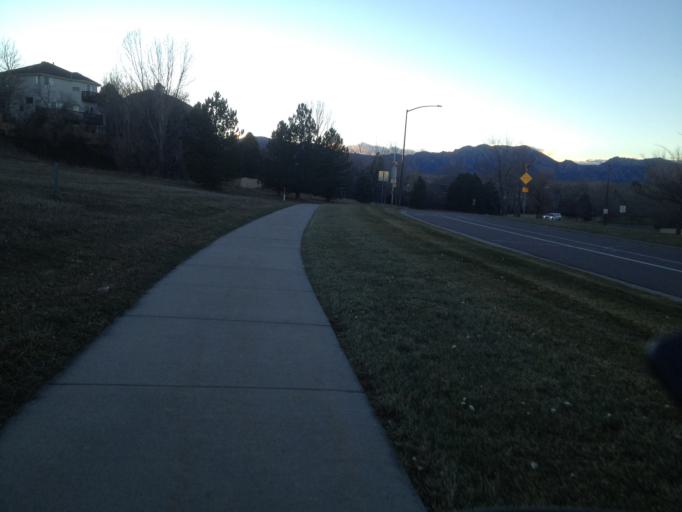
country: US
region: Colorado
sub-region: Boulder County
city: Superior
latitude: 39.9560
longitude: -105.1483
